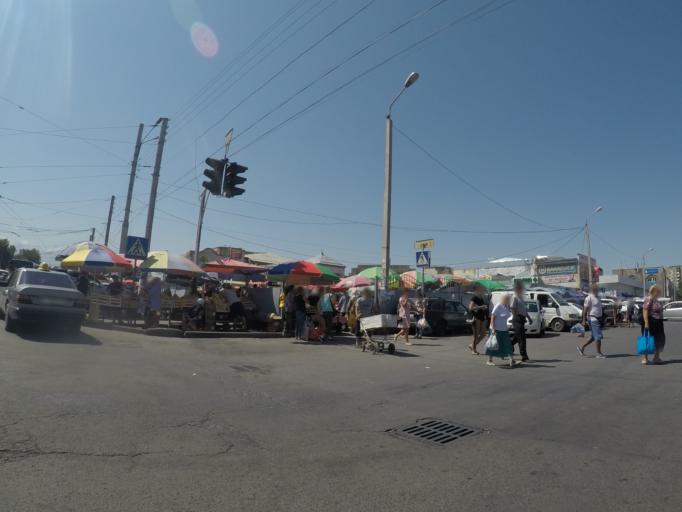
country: KG
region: Chuy
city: Bishkek
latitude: 42.8762
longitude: 74.5715
